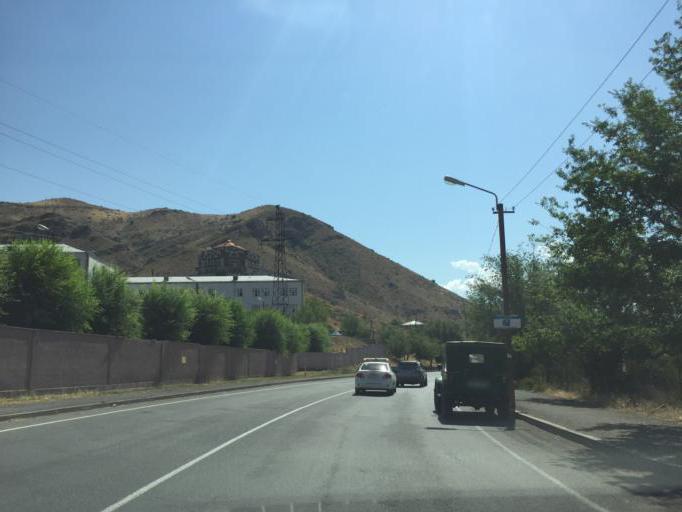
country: AM
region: Vayots' Dzori Marz
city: Vayk'
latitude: 39.6959
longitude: 45.4586
